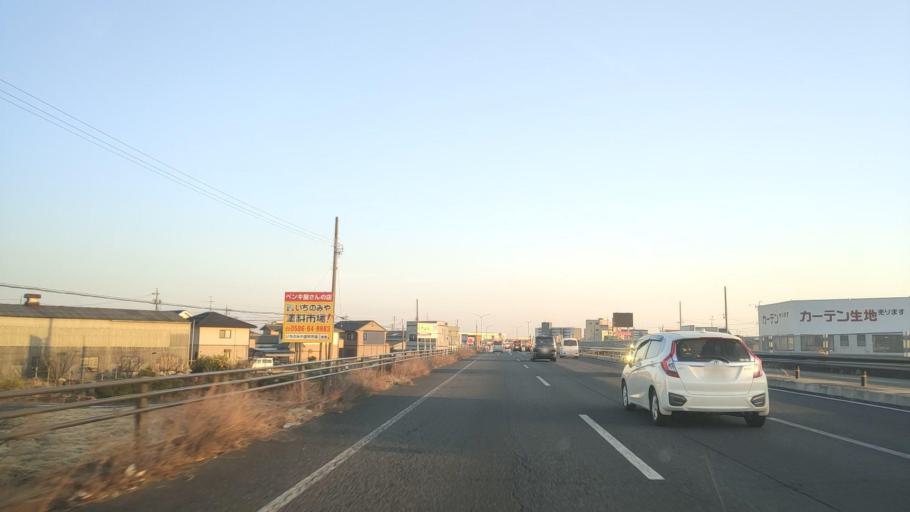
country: JP
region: Aichi
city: Kuroda
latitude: 35.3582
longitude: 136.7849
